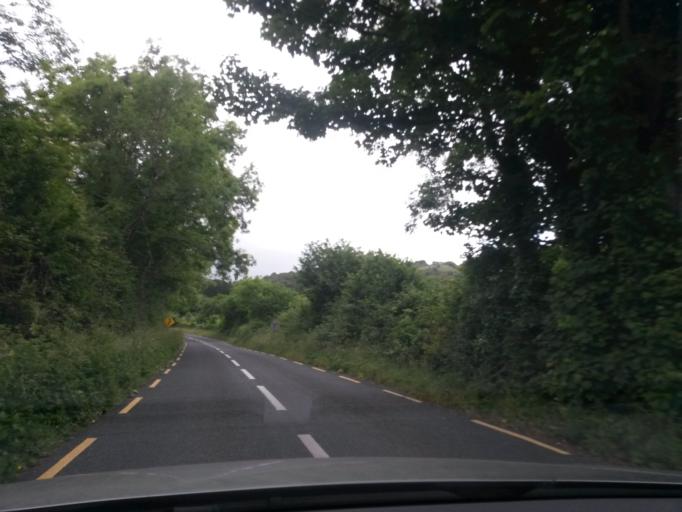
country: IE
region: Connaught
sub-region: County Leitrim
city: Manorhamilton
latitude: 54.2606
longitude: -8.3135
